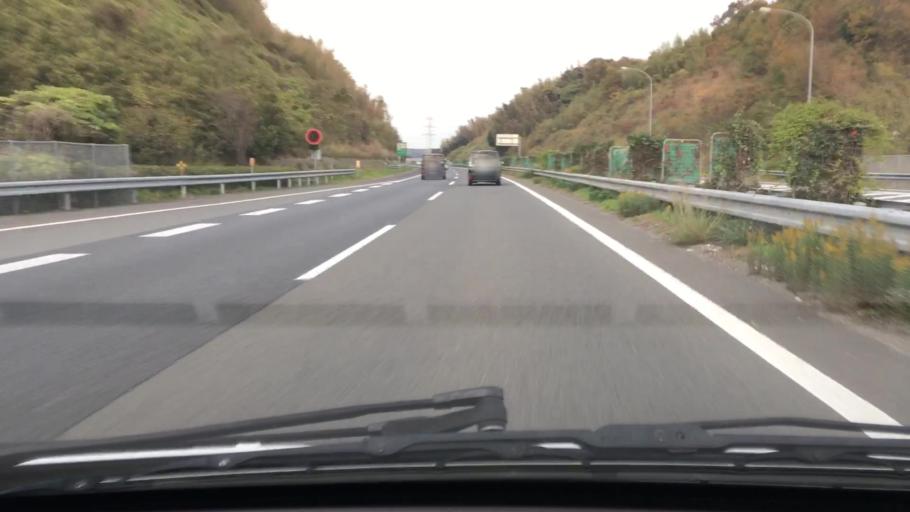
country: JP
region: Chiba
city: Kisarazu
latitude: 35.3867
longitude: 139.9986
